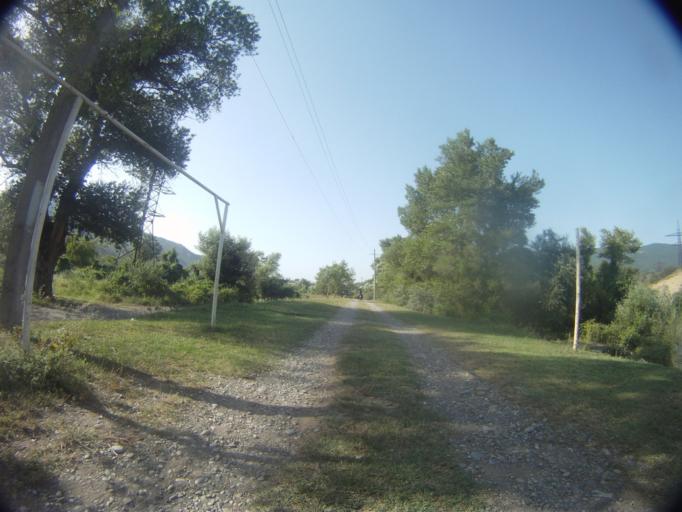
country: GE
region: Mtskheta-Mtianeti
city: Mtskheta
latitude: 41.8492
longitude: 44.7294
